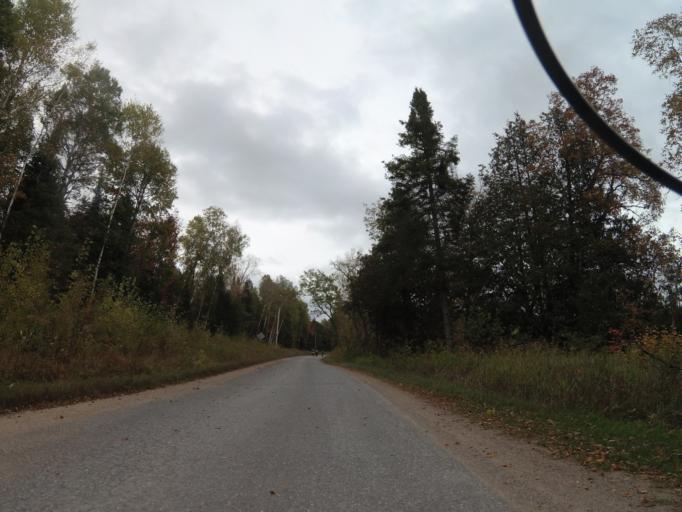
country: CA
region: Ontario
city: Renfrew
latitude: 45.2542
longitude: -77.1908
